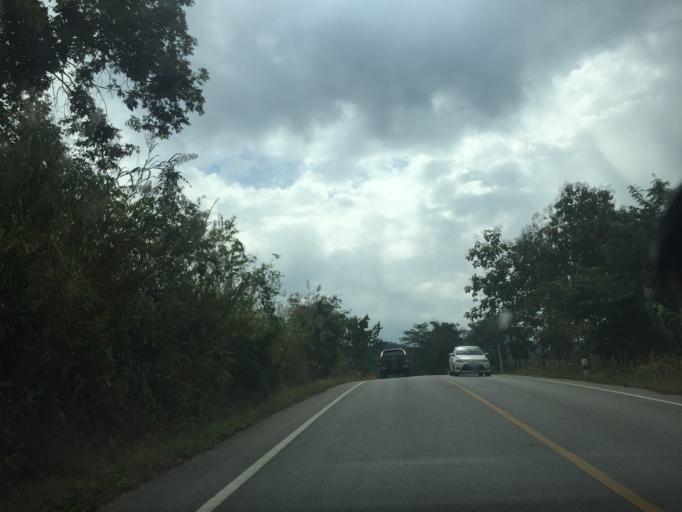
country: TH
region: Lampang
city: Mueang Pan
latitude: 18.7793
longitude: 99.5267
